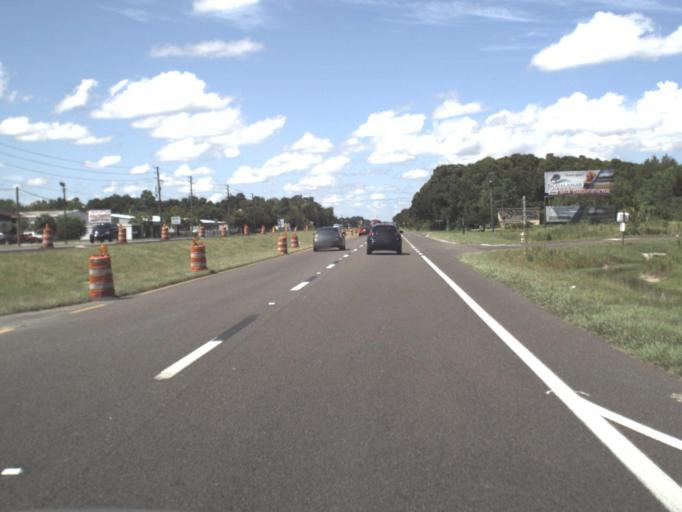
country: US
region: Florida
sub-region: Polk County
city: Fussels Corner
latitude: 28.0480
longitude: -81.8668
